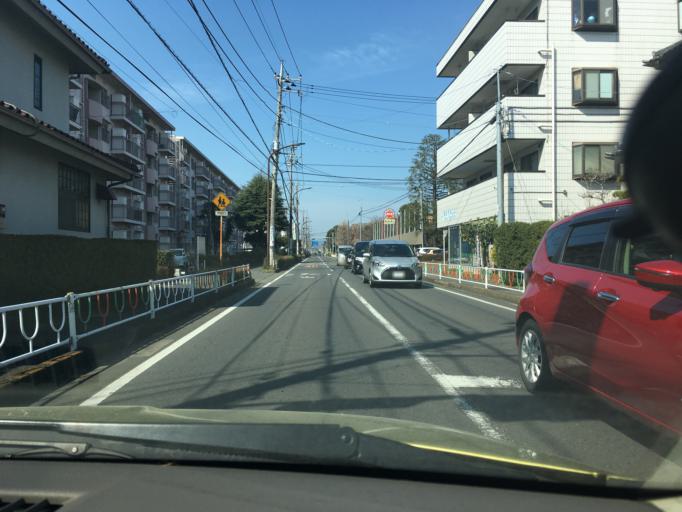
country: JP
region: Tokyo
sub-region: Machida-shi
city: Machida
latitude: 35.5671
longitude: 139.3806
